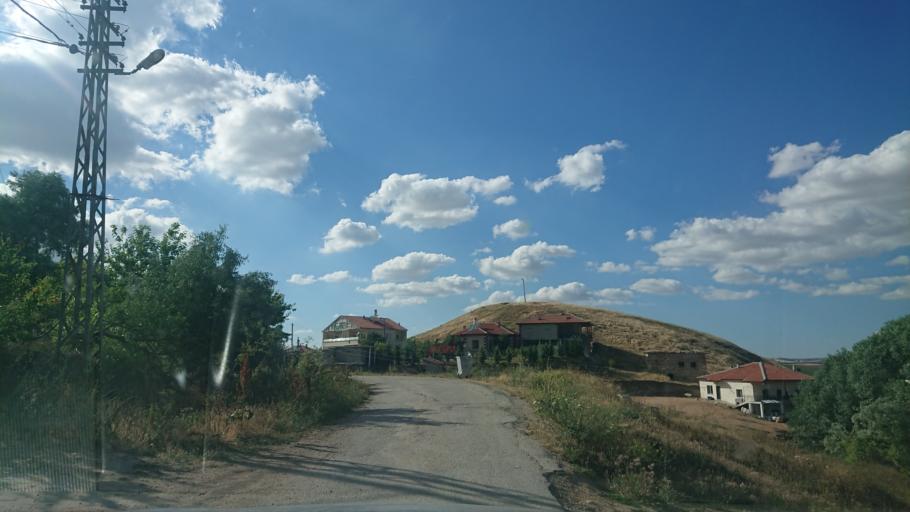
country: TR
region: Aksaray
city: Agacoren
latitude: 38.7531
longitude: 33.8865
